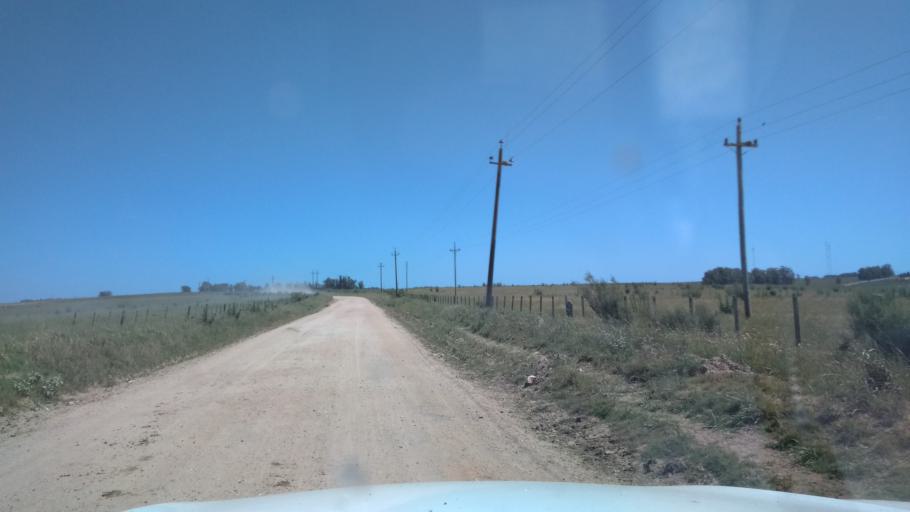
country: UY
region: Florida
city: Casupa
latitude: -34.0546
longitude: -55.8927
